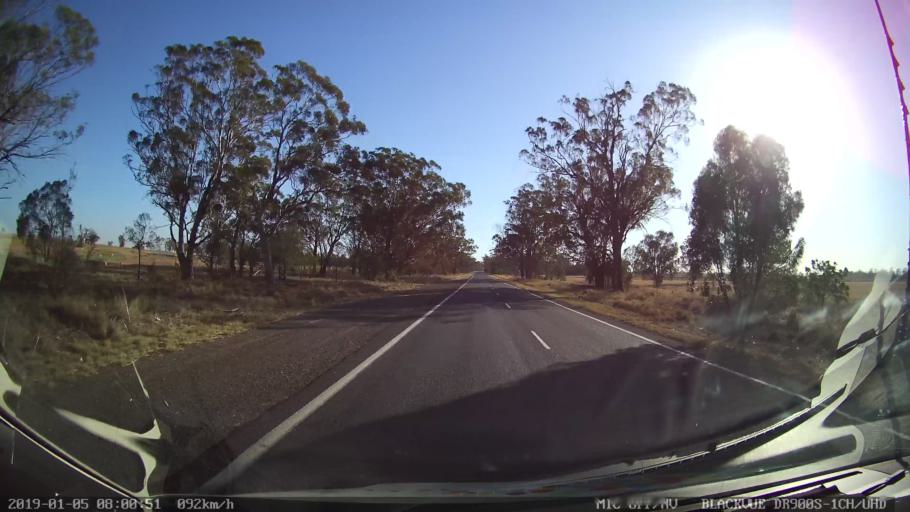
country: AU
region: New South Wales
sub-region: Gilgandra
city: Gilgandra
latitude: -31.6905
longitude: 148.6943
